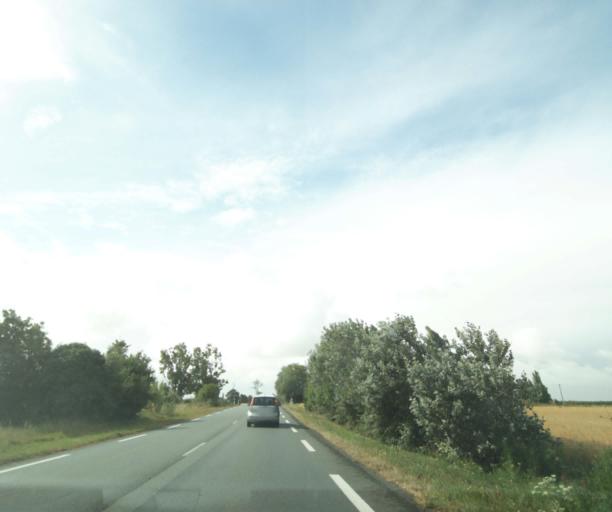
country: FR
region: Poitou-Charentes
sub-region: Departement de la Charente-Maritime
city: Charron
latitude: 46.2916
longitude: -1.0843
